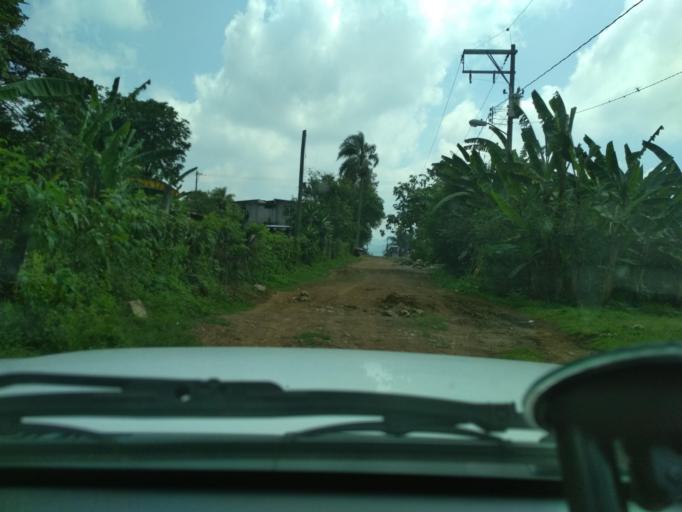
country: MX
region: Veracruz
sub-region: Fortin
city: Santa Lucia Potrerillo
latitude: 18.9681
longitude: -97.0265
